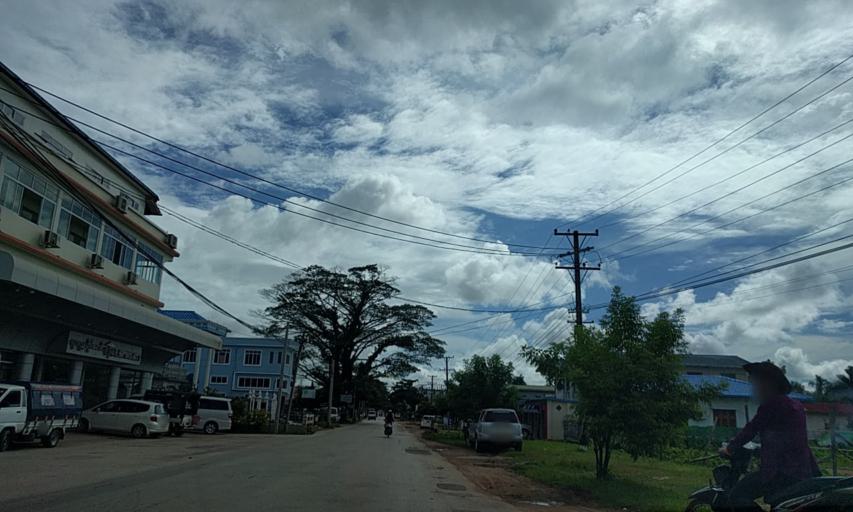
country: MM
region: Mon
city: Mawlamyine
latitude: 16.4601
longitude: 97.6480
